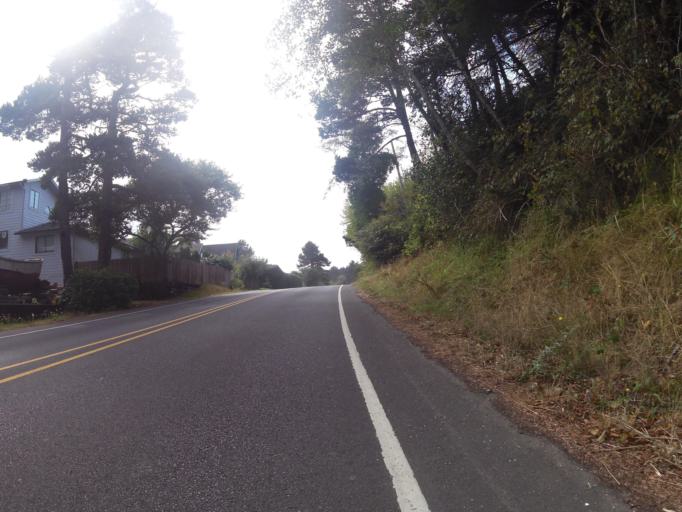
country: US
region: Oregon
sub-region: Lincoln County
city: Newport
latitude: 44.6536
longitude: -124.0565
